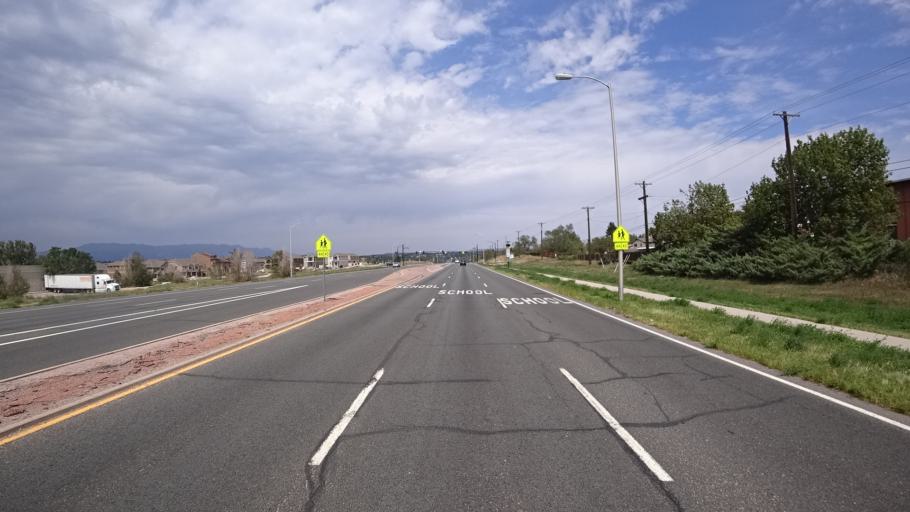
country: US
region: Colorado
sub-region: El Paso County
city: Stratmoor
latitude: 38.8089
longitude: -104.7801
